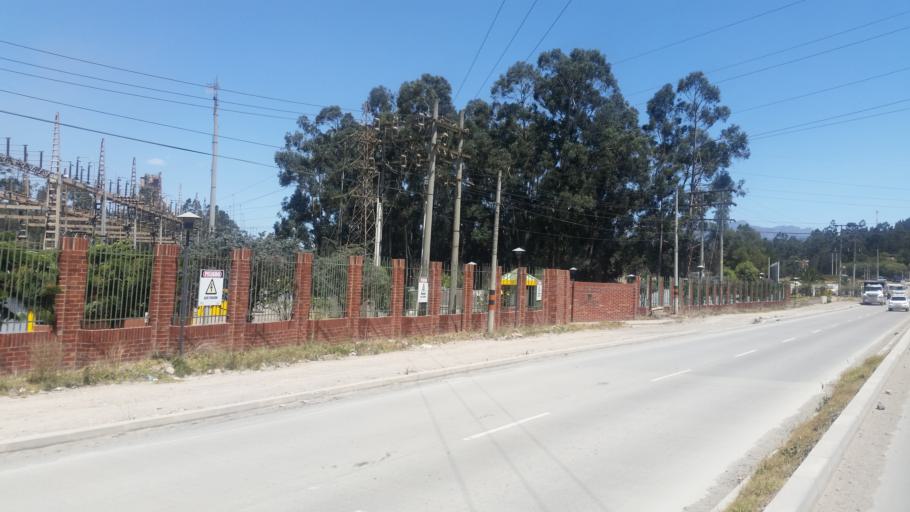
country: CO
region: Boyaca
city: Nobsa
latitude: 5.7582
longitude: -72.8925
